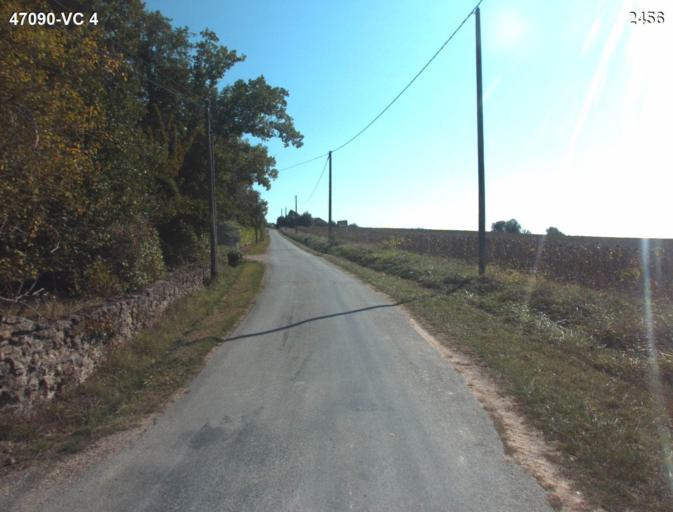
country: FR
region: Aquitaine
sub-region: Departement du Lot-et-Garonne
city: Nerac
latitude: 44.1736
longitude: 0.3685
